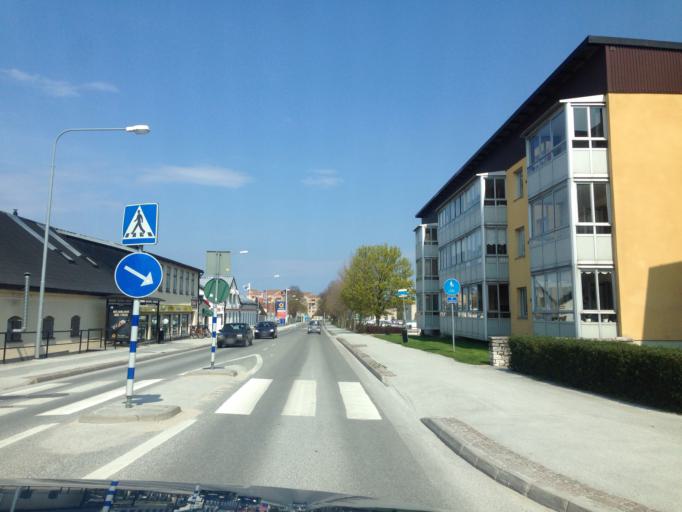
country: SE
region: Gotland
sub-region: Gotland
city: Visby
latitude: 57.6281
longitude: 18.2875
